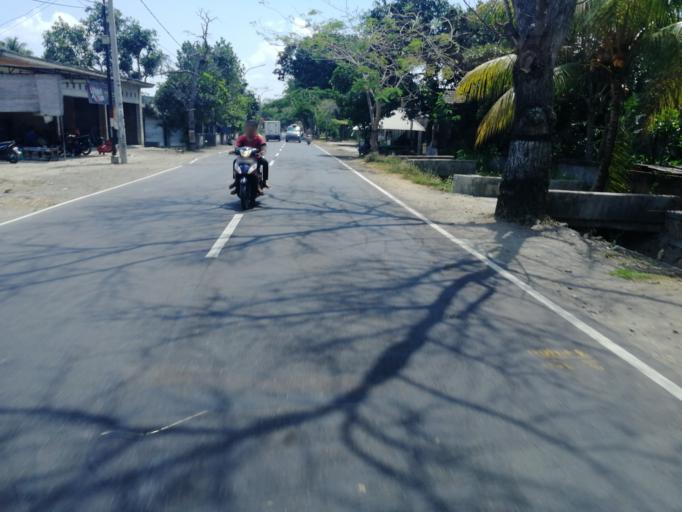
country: ID
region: West Nusa Tenggara
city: Jelateng Timur
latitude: -8.7063
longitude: 116.0857
